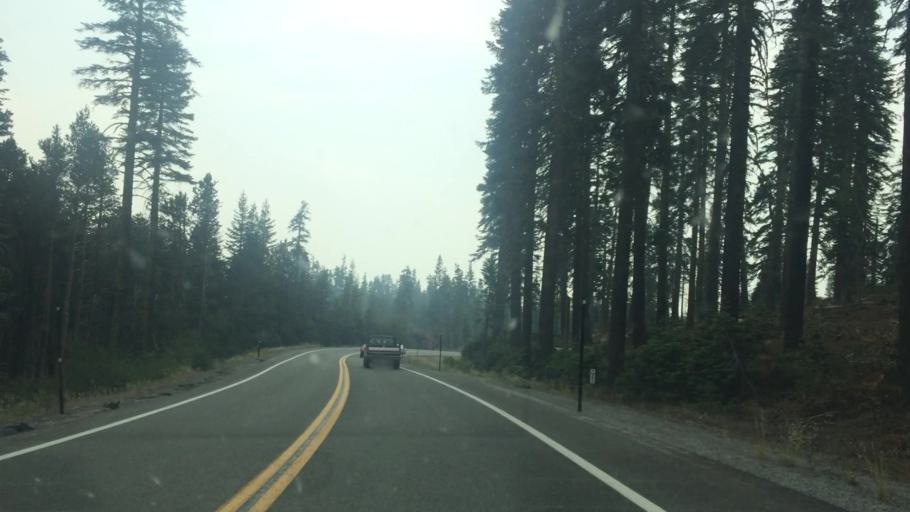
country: US
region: California
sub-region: El Dorado County
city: South Lake Tahoe
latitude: 38.6252
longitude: -120.2147
